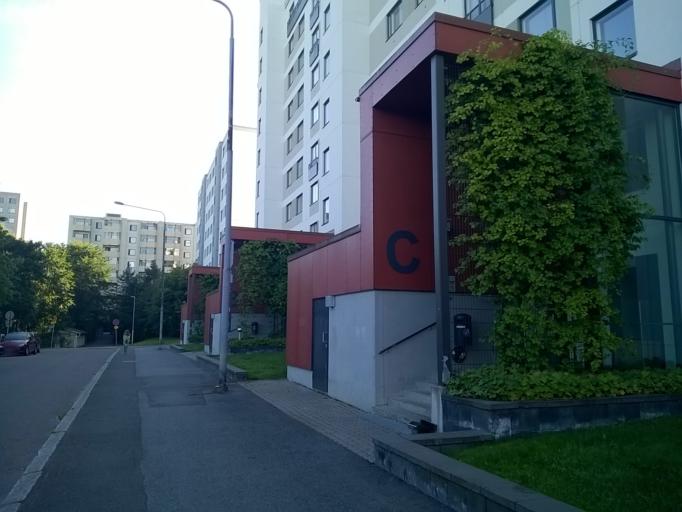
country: FI
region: Pirkanmaa
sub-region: Tampere
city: Tampere
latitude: 61.4446
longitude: 23.8495
